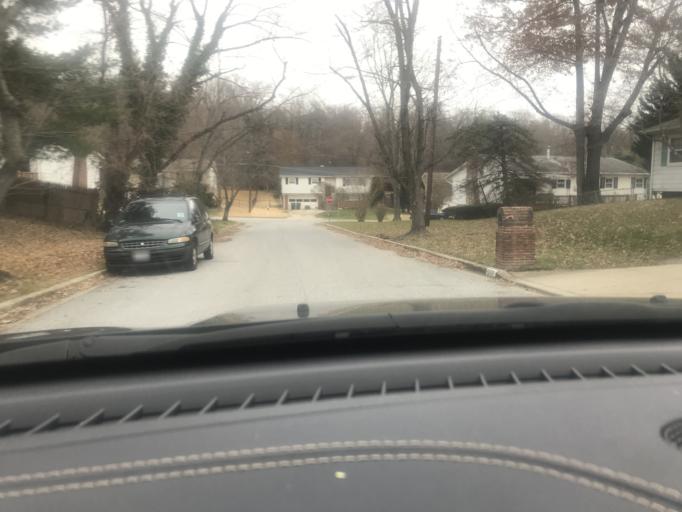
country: US
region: Maryland
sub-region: Prince George's County
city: Oxon Hill
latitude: 38.7967
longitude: -76.9699
